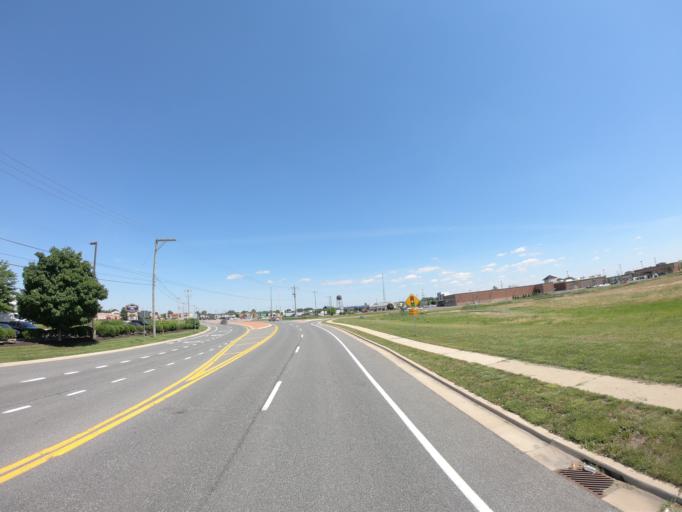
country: US
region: Delaware
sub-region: New Castle County
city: Middletown
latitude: 39.4506
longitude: -75.7308
